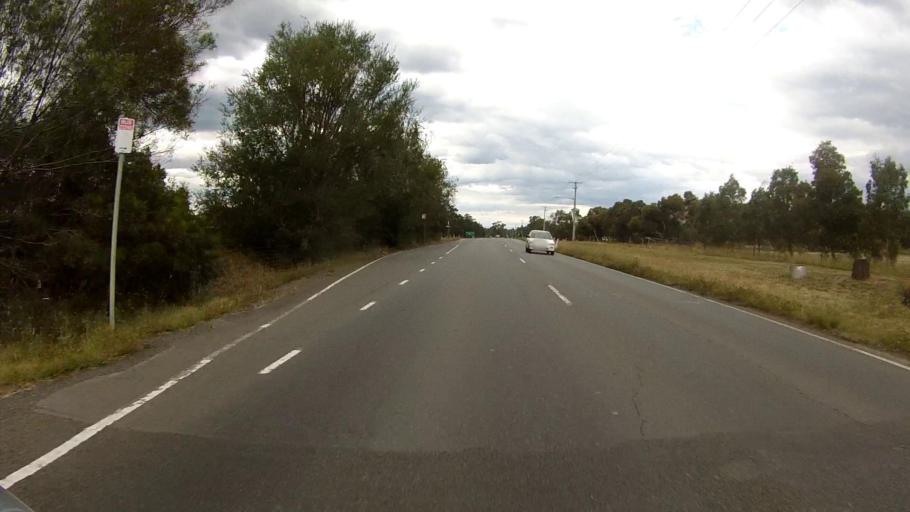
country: AU
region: Tasmania
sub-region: Clarence
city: Cambridge
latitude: -42.8428
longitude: 147.4730
